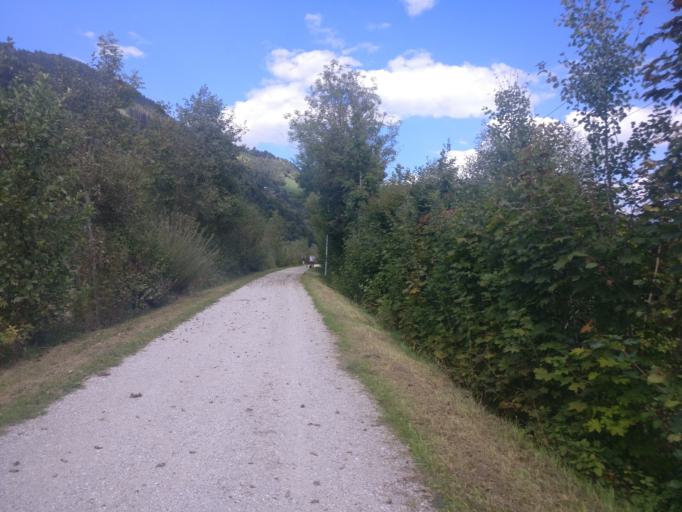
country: AT
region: Salzburg
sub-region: Politischer Bezirk Sankt Johann im Pongau
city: Sankt Johann im Pongau
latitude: 47.3708
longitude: 13.2104
